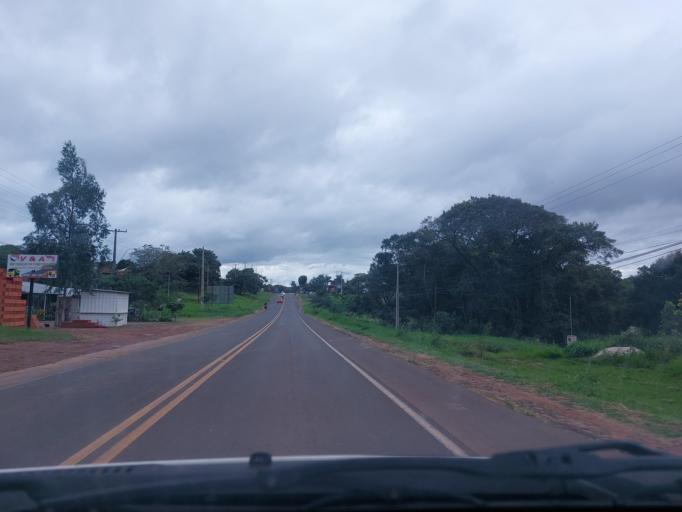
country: PY
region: San Pedro
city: Guayaybi
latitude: -24.6636
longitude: -56.4263
